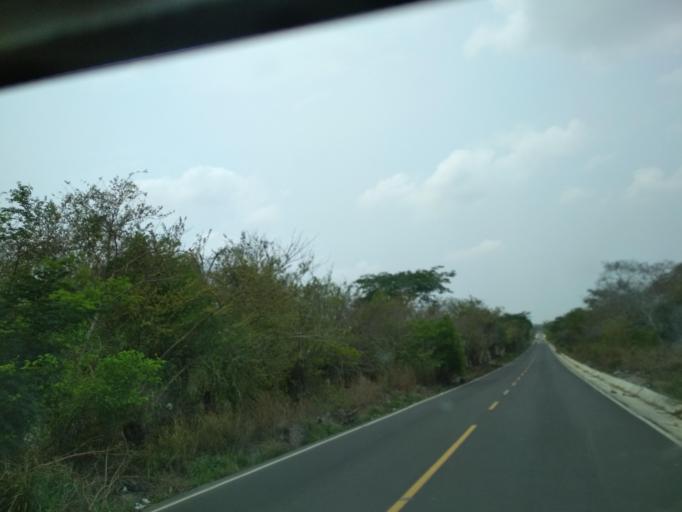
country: MX
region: Veracruz
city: Manlio Fabio Altamirano
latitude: 19.1413
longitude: -96.2994
